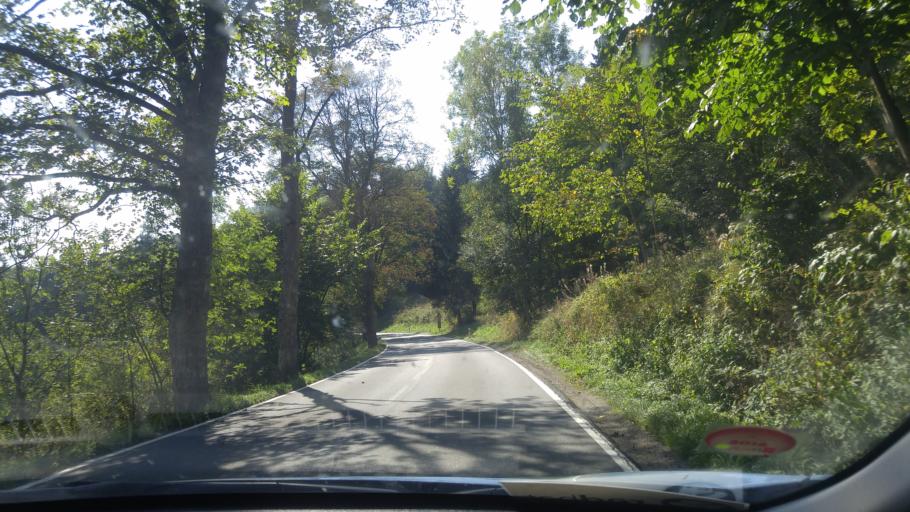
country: CZ
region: Olomoucky
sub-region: Okres Sumperk
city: Stare Mesto
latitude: 50.1675
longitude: 17.0276
